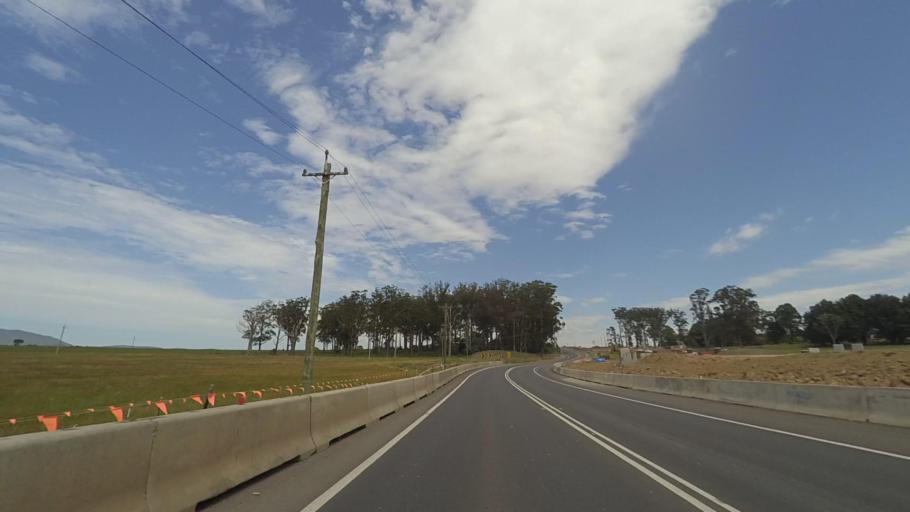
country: AU
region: New South Wales
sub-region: Shoalhaven Shire
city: Berry
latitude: -34.7806
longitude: 150.6806
